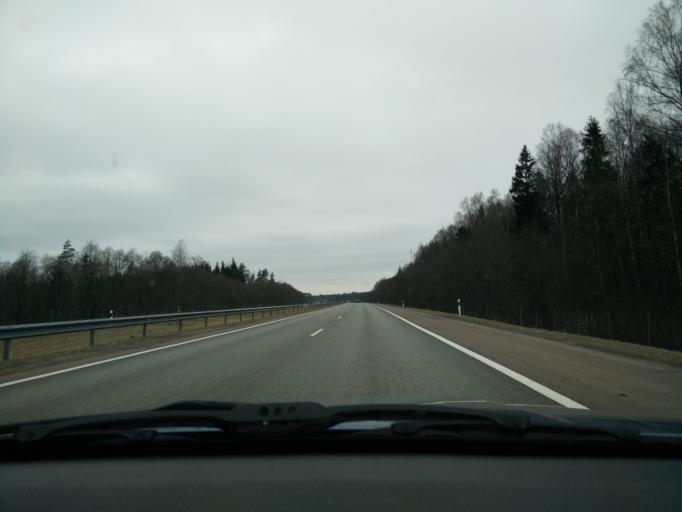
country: LT
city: Rietavas
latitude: 55.6428
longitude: 21.8831
